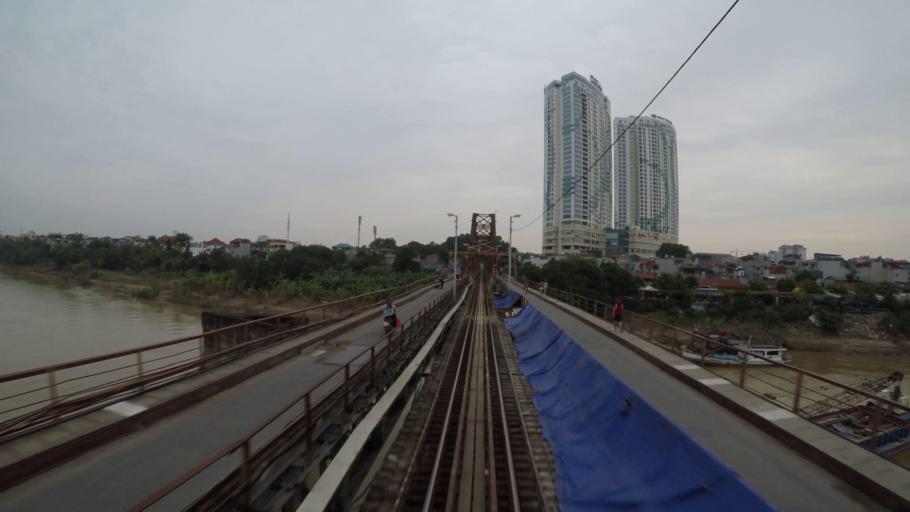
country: VN
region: Ha Noi
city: Hoan Kiem
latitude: 21.0528
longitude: 105.8893
